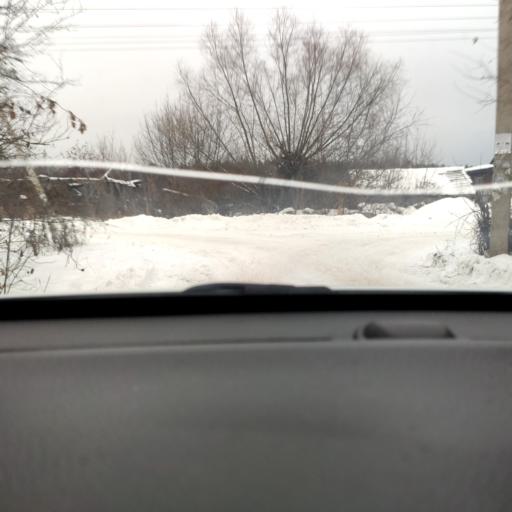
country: RU
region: Voronezj
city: Volya
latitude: 51.7517
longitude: 39.4978
